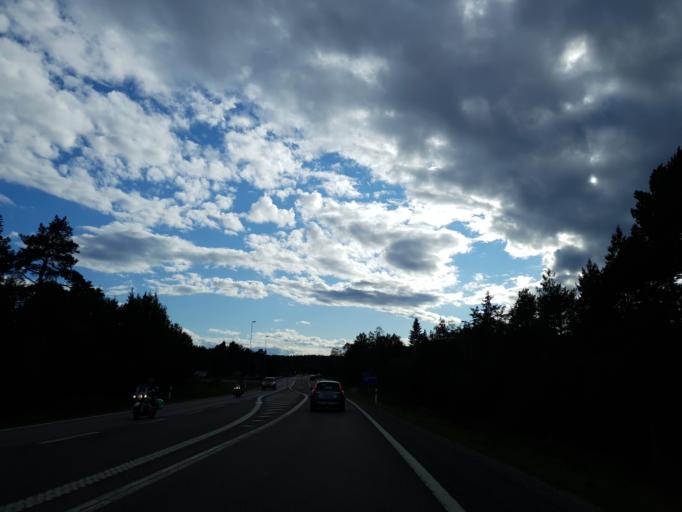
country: SE
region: Vaesternorrland
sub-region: Timra Kommun
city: Soraker
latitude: 62.5571
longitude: 17.6454
